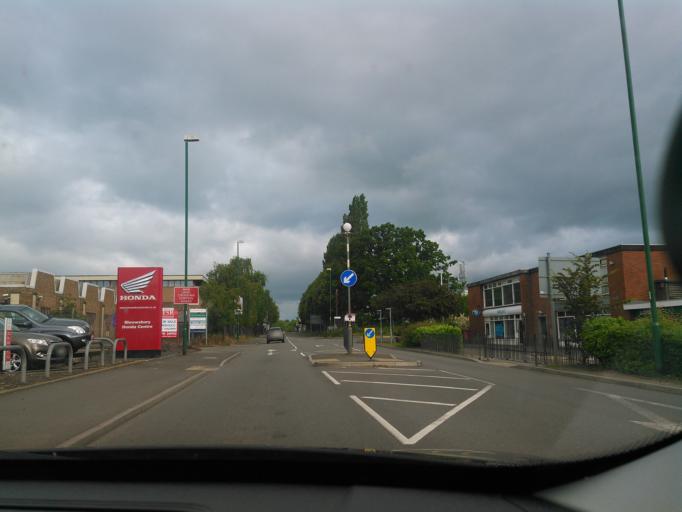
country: GB
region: England
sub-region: Shropshire
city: Shrewsbury
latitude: 52.7371
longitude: -2.7259
